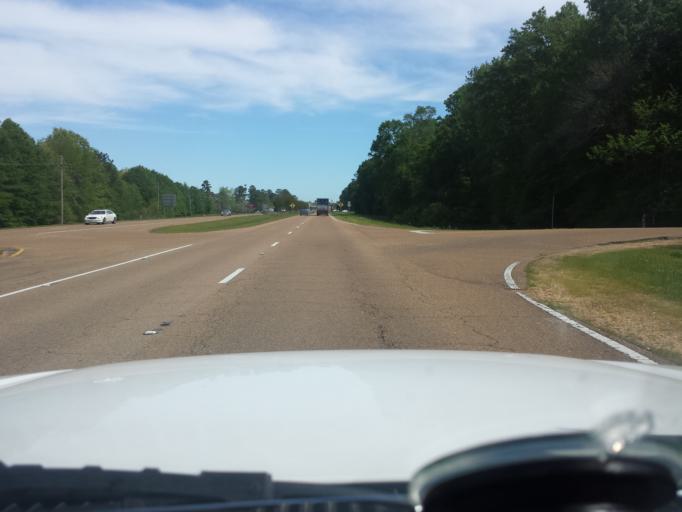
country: US
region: Mississippi
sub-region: Rankin County
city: Flowood
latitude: 32.3251
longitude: -90.0913
